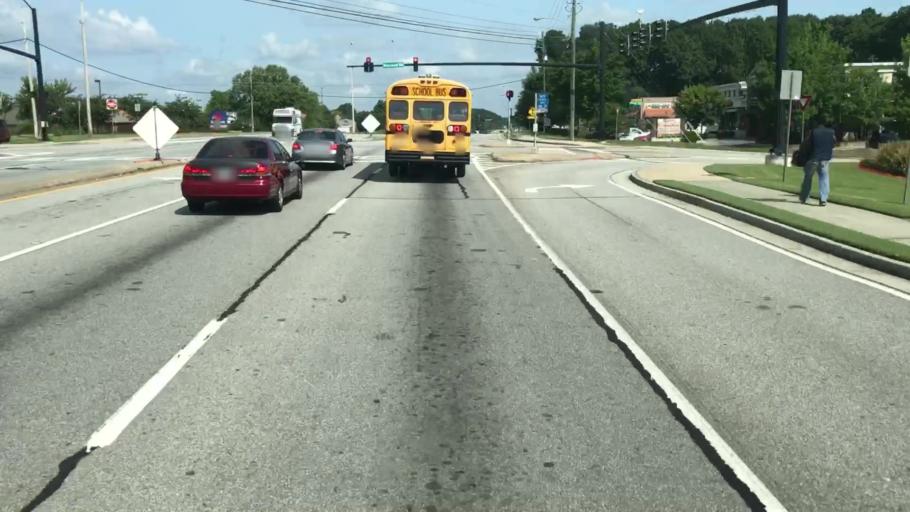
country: US
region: Georgia
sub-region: Gwinnett County
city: Grayson
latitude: 33.8968
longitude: -83.9588
